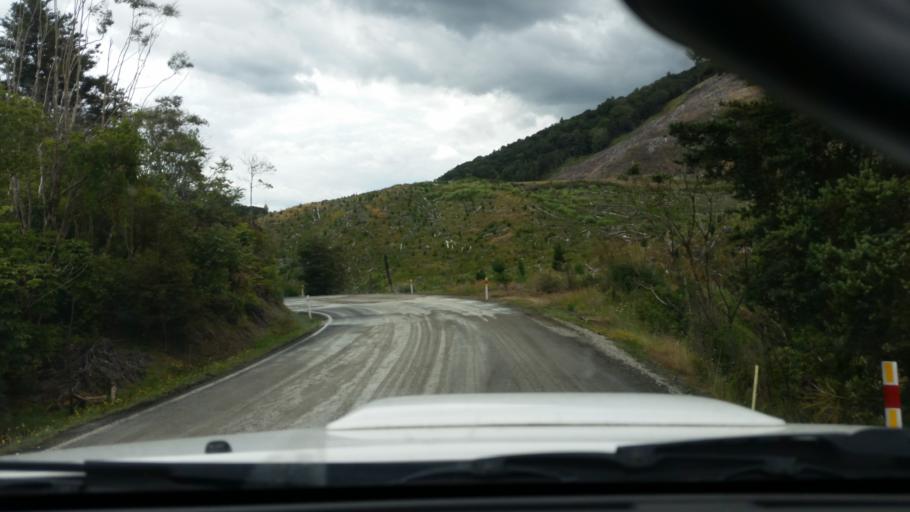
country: NZ
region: Northland
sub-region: Kaipara District
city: Dargaville
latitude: -35.7200
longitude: 173.8588
